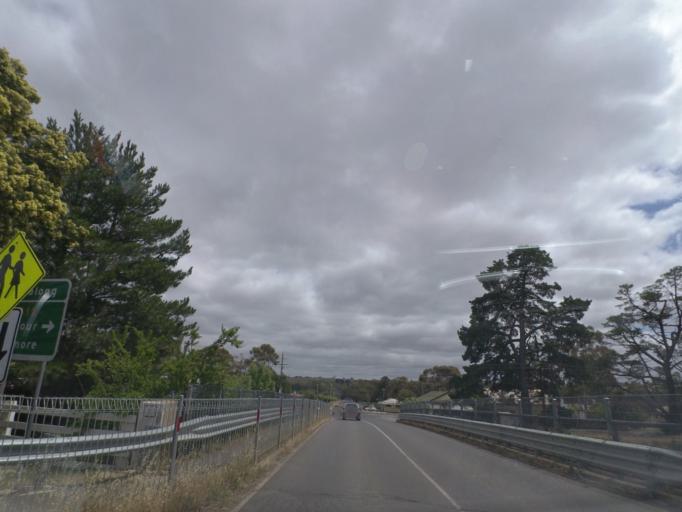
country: AU
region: Victoria
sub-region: Whittlesea
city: Whittlesea
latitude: -37.2063
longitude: 145.0461
